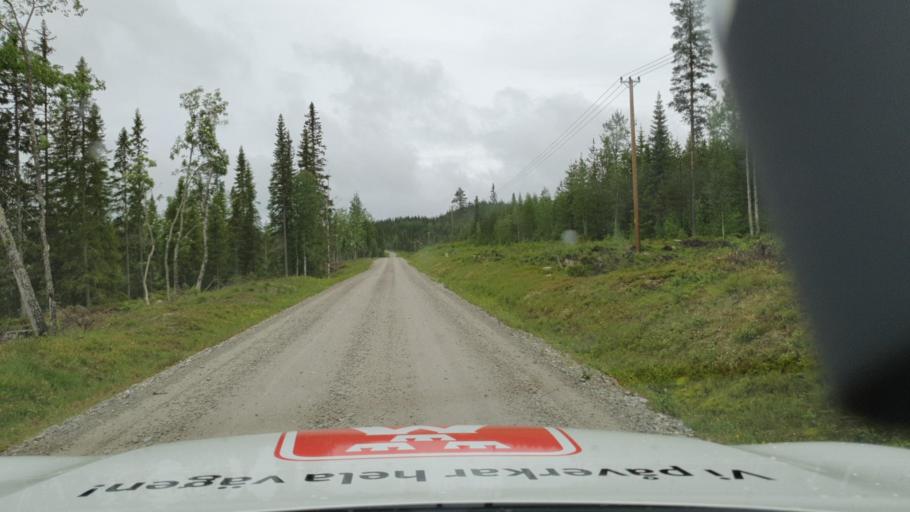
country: SE
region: Vaesterbotten
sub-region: Asele Kommun
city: Asele
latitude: 63.9702
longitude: 16.8774
